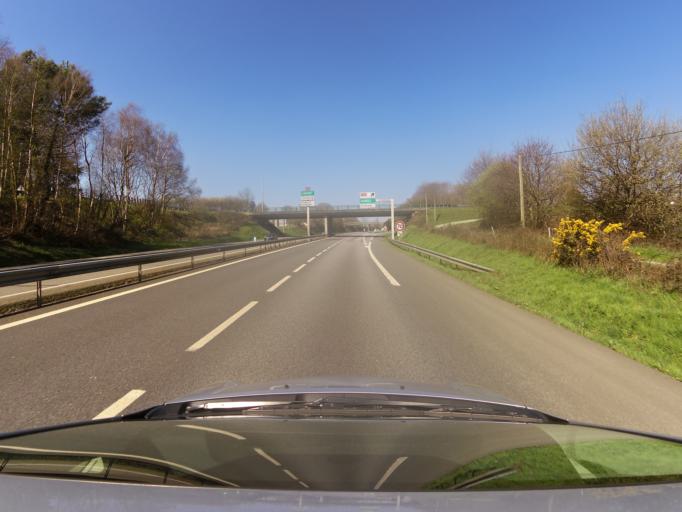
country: FR
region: Brittany
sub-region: Departement du Morbihan
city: Ploermel
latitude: 47.9186
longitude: -2.4029
